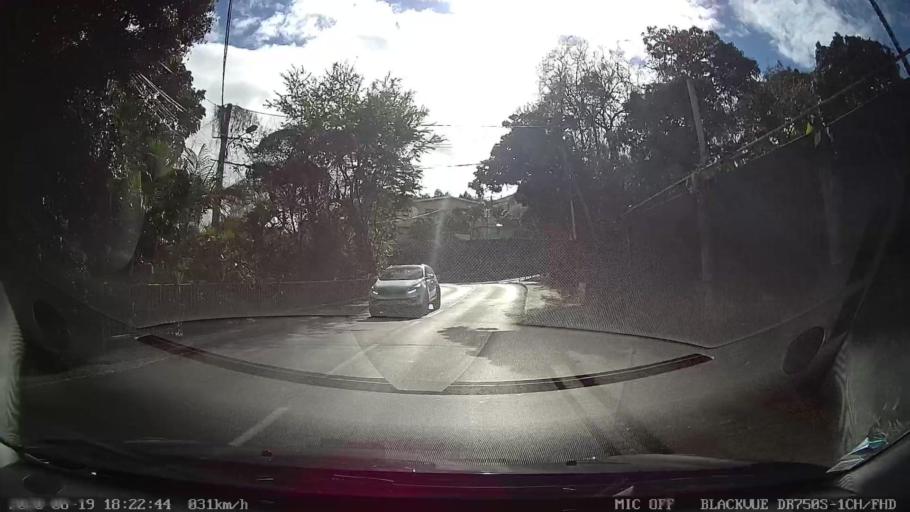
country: RE
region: Reunion
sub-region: Reunion
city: La Possession
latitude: -20.9539
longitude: 55.3399
